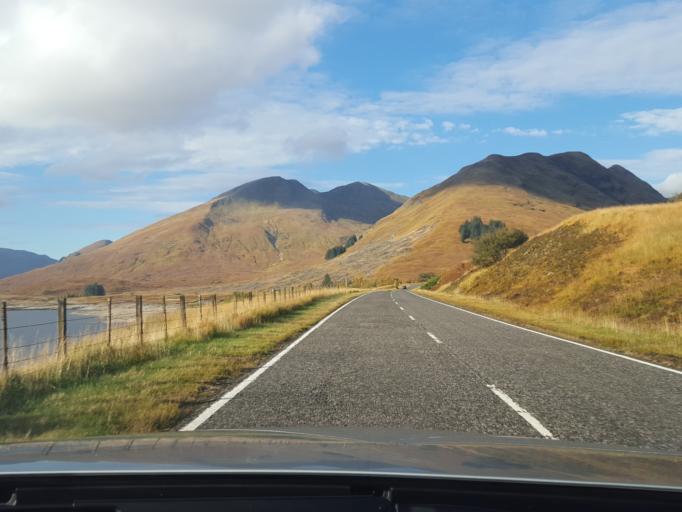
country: GB
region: Scotland
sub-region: Highland
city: Fort William
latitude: 57.1568
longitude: -5.1481
